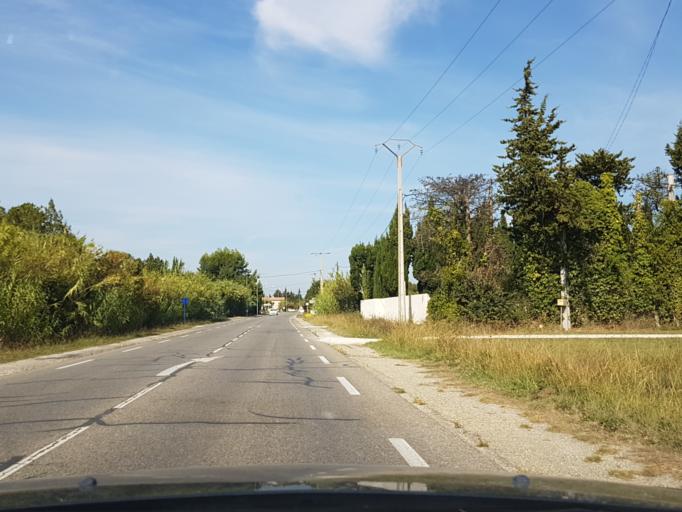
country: FR
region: Provence-Alpes-Cote d'Azur
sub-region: Departement des Bouches-du-Rhone
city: Noves
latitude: 43.8706
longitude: 4.8989
